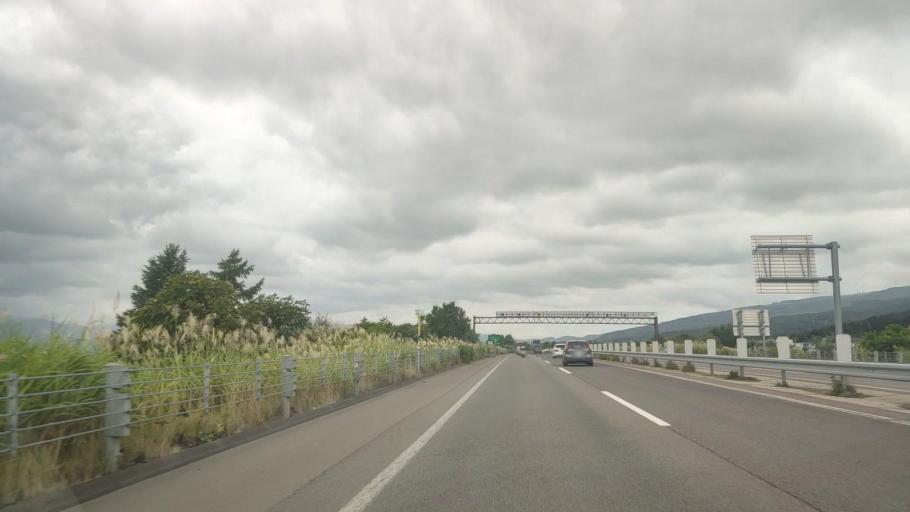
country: JP
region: Hokkaido
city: Nanae
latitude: 41.8601
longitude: 140.7340
